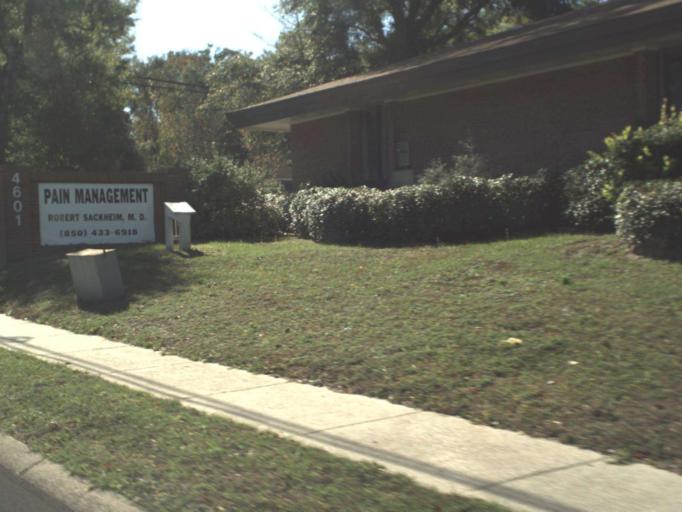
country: US
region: Florida
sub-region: Escambia County
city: Brent
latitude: 30.4649
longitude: -87.2142
